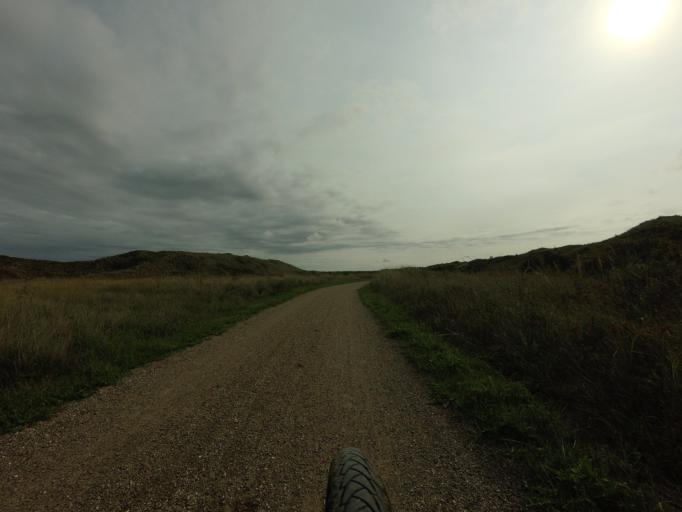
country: DK
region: North Denmark
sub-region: Hjorring Kommune
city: Sindal
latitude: 57.5884
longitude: 10.1337
